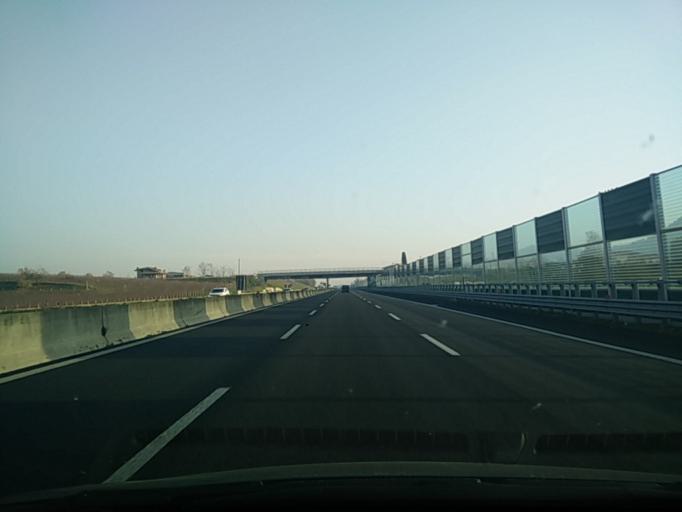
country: IT
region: Lombardy
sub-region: Provincia di Brescia
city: Adro
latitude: 45.6052
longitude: 9.9456
